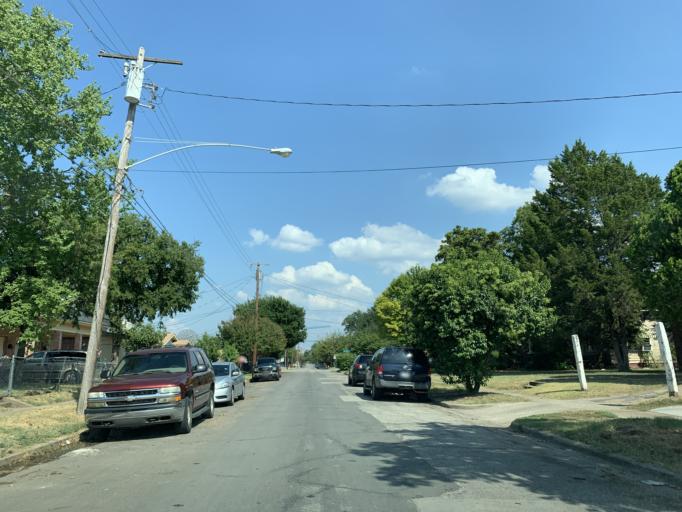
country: US
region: Texas
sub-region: Dallas County
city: Dallas
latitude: 32.7464
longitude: -96.8332
